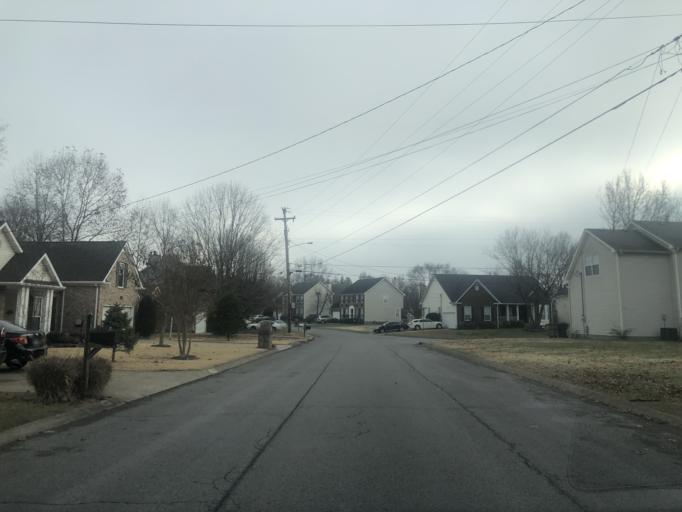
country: US
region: Tennessee
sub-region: Rutherford County
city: La Vergne
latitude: 36.0730
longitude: -86.6544
